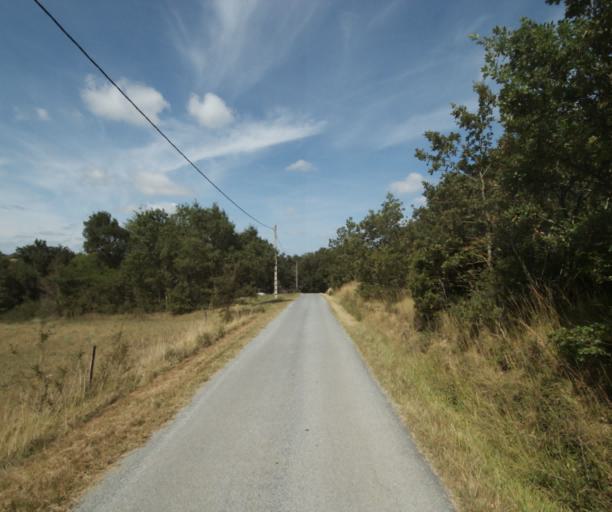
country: FR
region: Midi-Pyrenees
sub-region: Departement du Tarn
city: Dourgne
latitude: 43.4755
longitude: 2.1125
